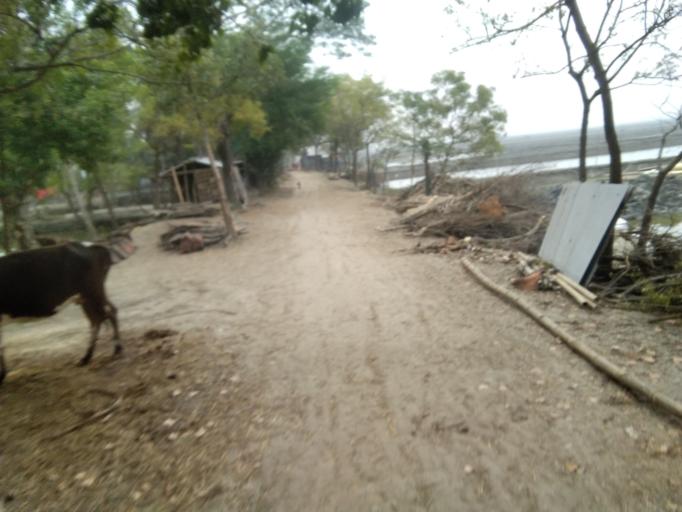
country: BD
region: Khulna
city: Satkhira
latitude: 22.5715
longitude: 89.0772
